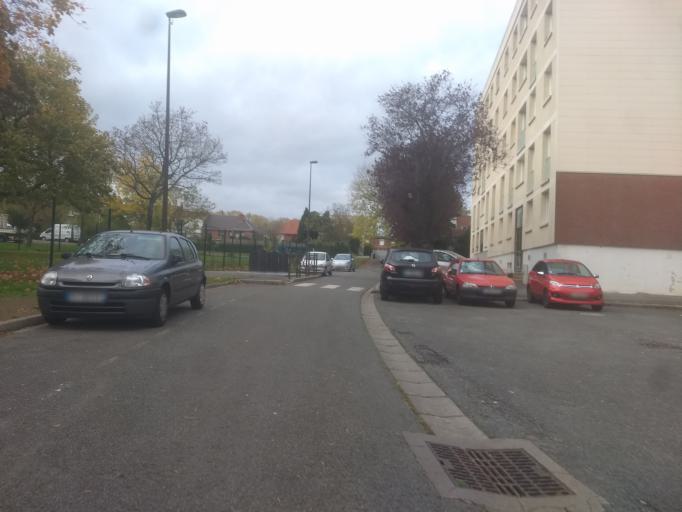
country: FR
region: Nord-Pas-de-Calais
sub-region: Departement du Pas-de-Calais
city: Achicourt
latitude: 50.2916
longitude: 2.7466
